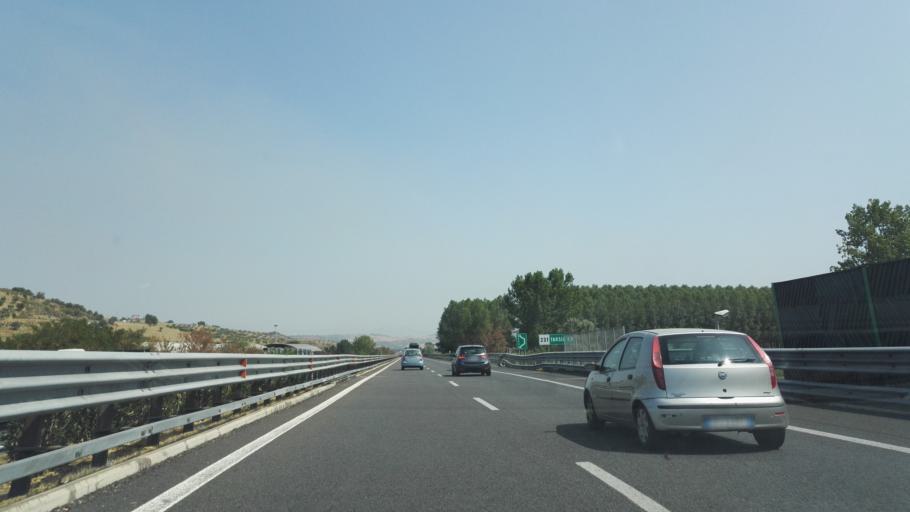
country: IT
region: Calabria
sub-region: Provincia di Cosenza
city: Sartano
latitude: 39.5379
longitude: 16.2238
